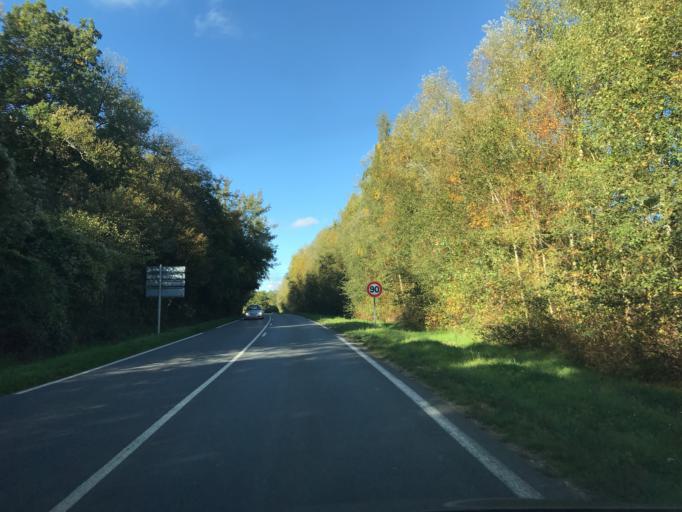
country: FR
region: Haute-Normandie
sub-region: Departement de l'Eure
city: Saint-Aubin-sur-Gaillon
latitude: 49.1216
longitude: 1.3107
